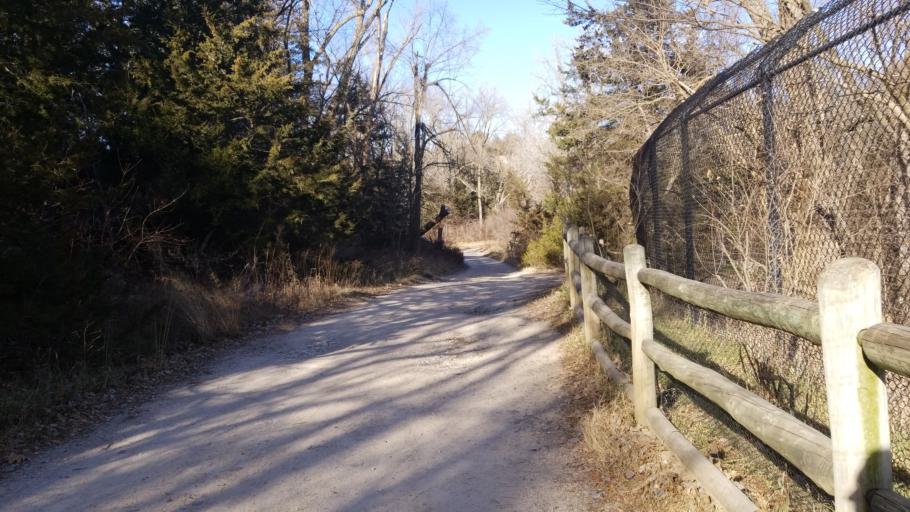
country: US
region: Nebraska
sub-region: Saunders County
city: Ashland
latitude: 41.0151
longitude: -96.2904
